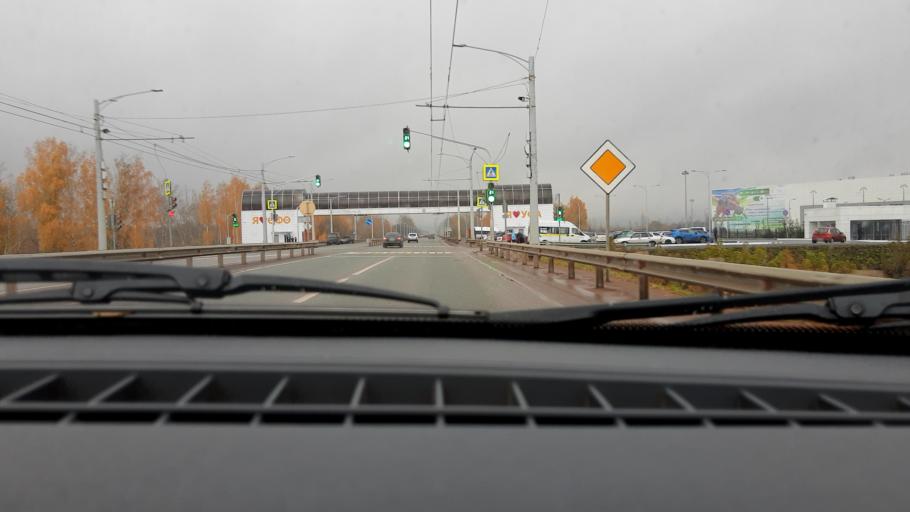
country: RU
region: Bashkortostan
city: Mikhaylovka
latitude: 54.7699
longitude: 55.9108
